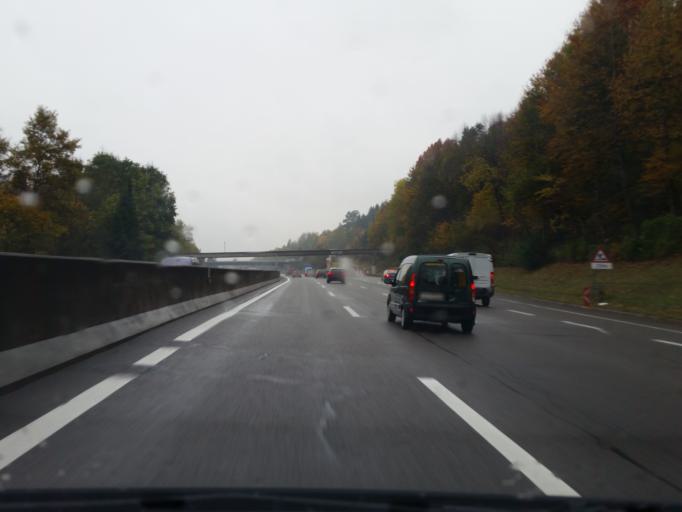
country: CH
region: Zurich
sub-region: Bezirk Winterthur
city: Toss
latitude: 47.4543
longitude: 8.7053
